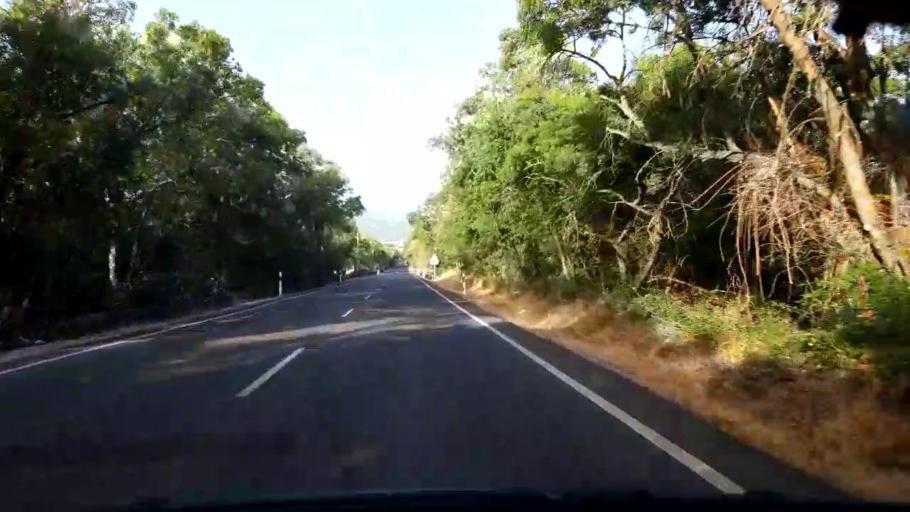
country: ES
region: Madrid
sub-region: Provincia de Madrid
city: Guadarrama
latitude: 40.6835
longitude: -4.0649
